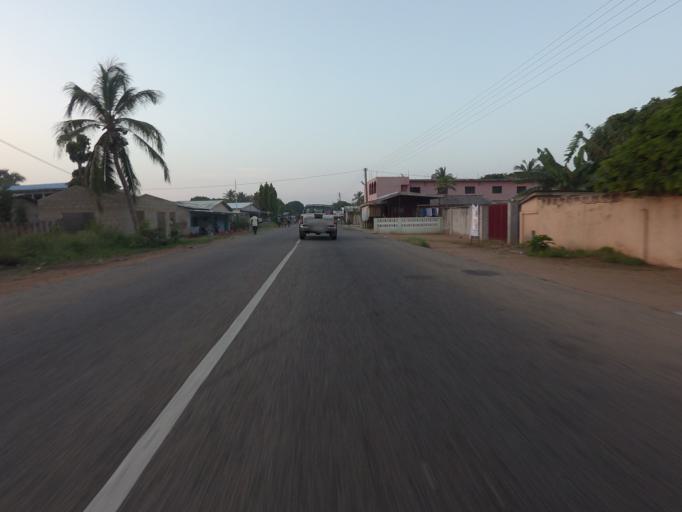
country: GH
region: Volta
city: Keta
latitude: 5.8616
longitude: 0.9781
